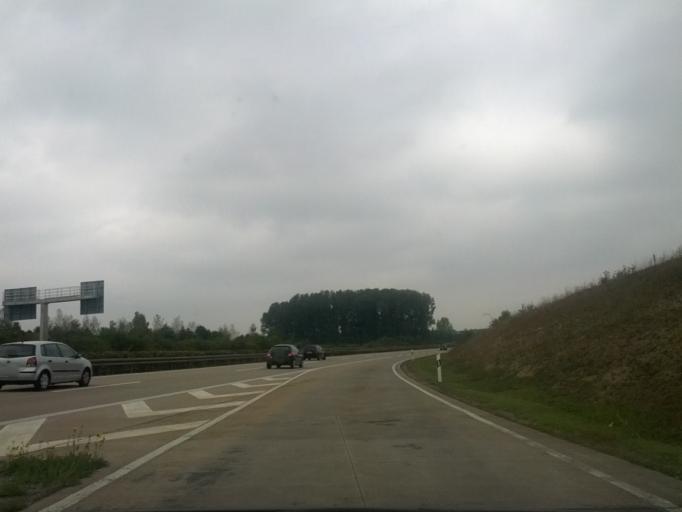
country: DE
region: Thuringia
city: Ichtershausen
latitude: 50.8964
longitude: 10.9510
